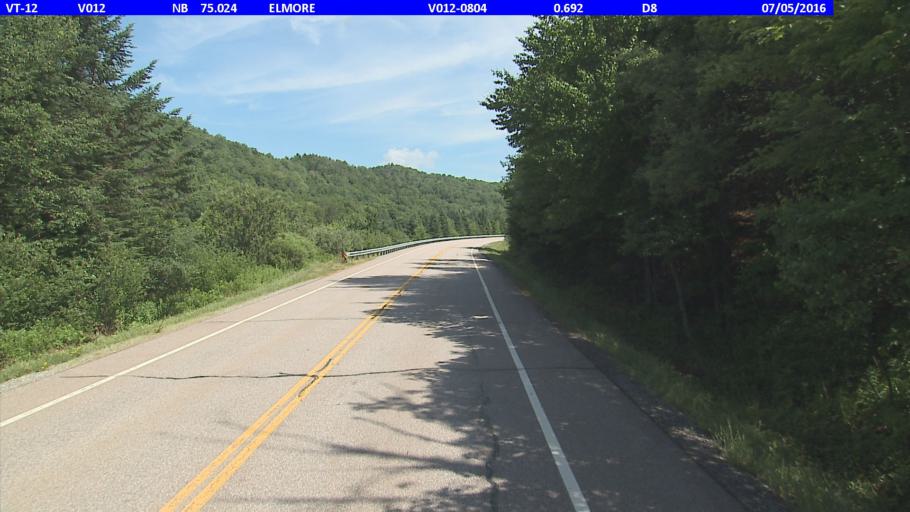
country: US
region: Vermont
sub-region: Lamoille County
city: Morrisville
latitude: 44.4617
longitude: -72.5449
